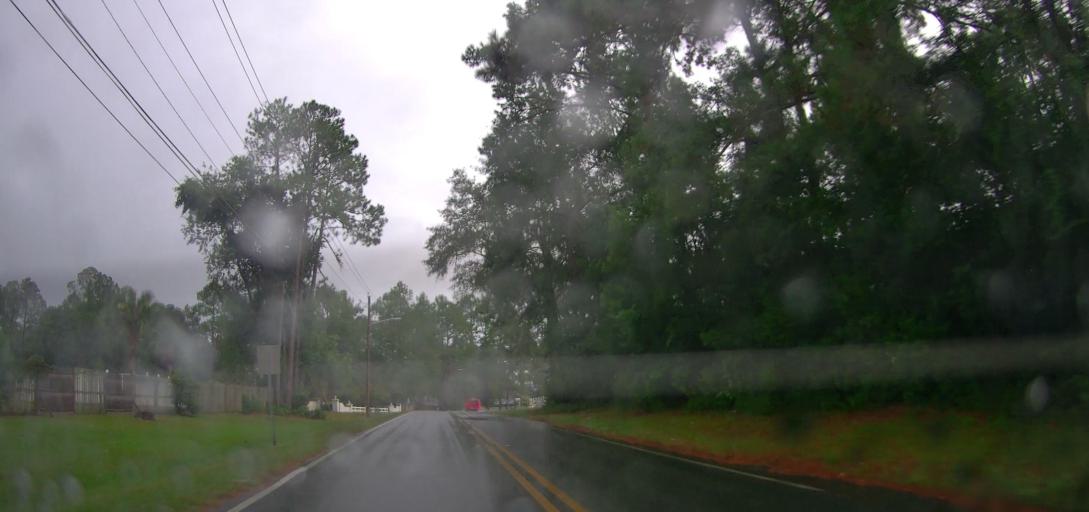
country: US
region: Georgia
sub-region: Ware County
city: Sunnyside
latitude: 31.2172
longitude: -82.3293
